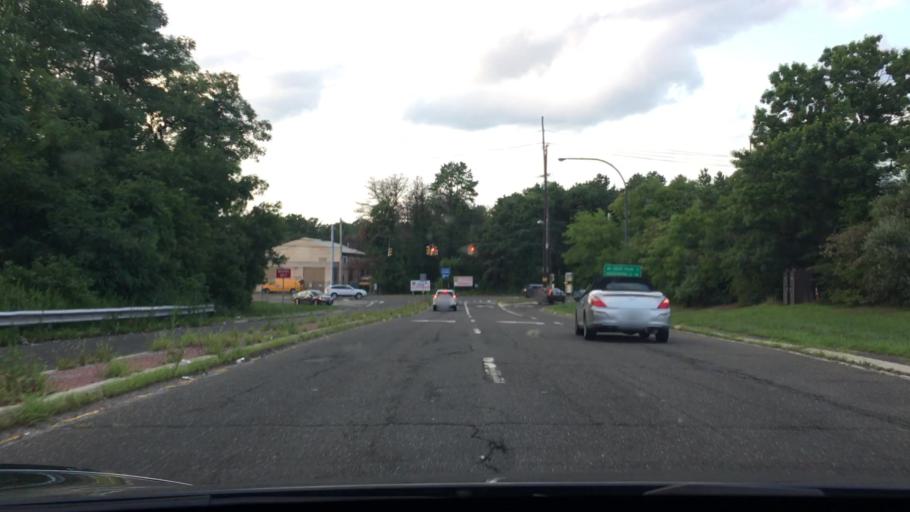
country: US
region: New York
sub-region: Suffolk County
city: Bay Wood
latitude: 40.7708
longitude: -73.2803
